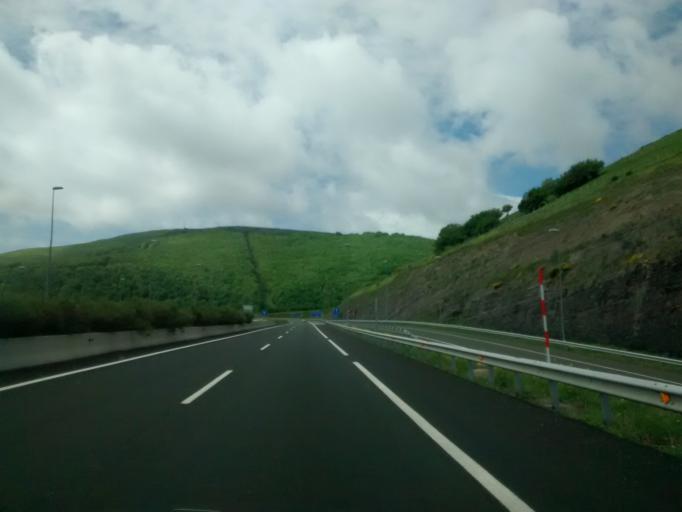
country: ES
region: Cantabria
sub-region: Provincia de Cantabria
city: Santiurde de Reinosa
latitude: 43.0662
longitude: -4.0882
